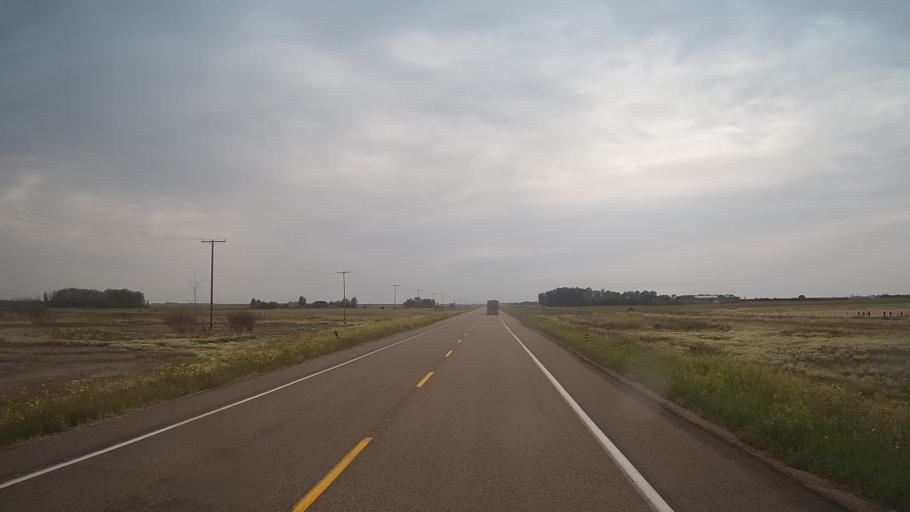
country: CA
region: Saskatchewan
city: Langham
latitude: 52.1289
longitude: -107.1325
